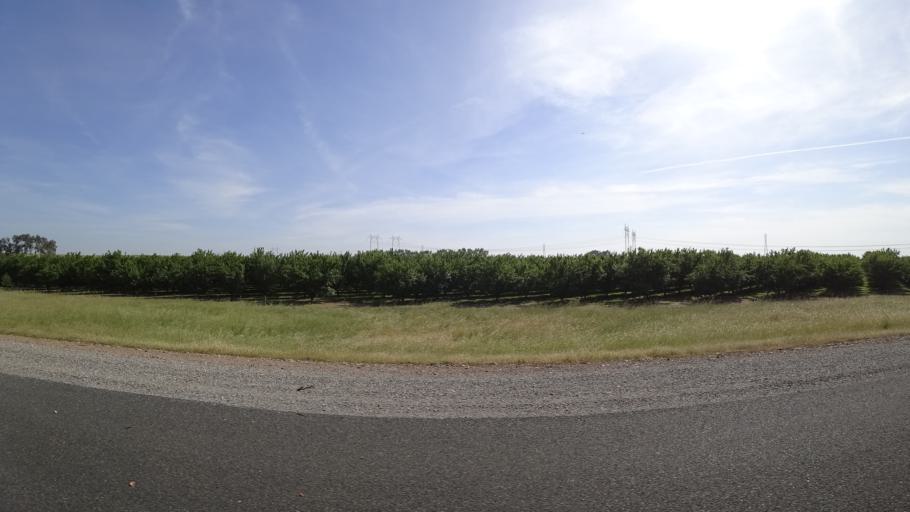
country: US
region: California
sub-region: Butte County
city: Thermalito
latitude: 39.6024
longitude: -121.6650
